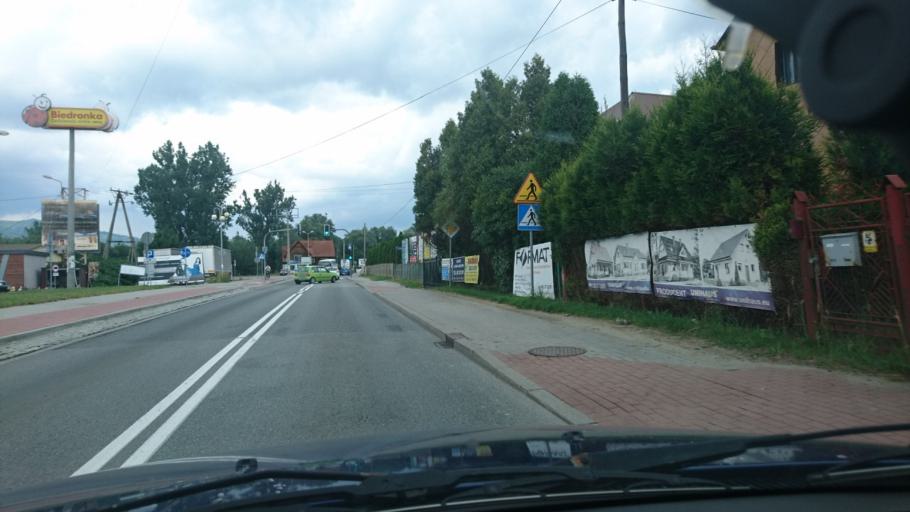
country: PL
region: Silesian Voivodeship
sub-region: Powiat zywiecki
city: Milowka
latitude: 49.5684
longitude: 19.0910
